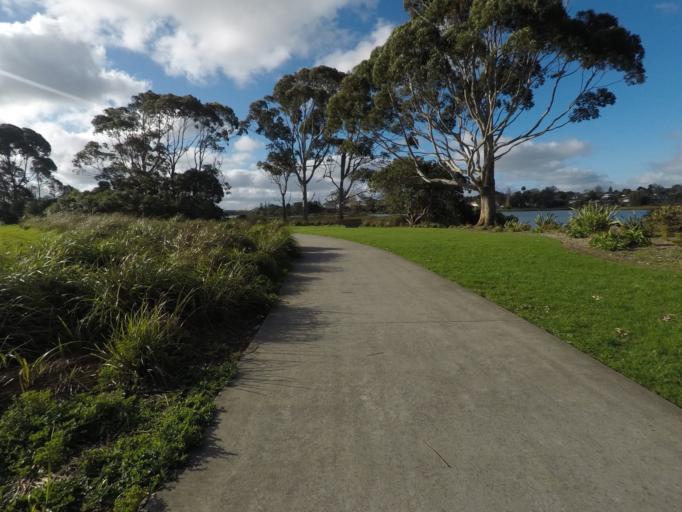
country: NZ
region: Auckland
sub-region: Auckland
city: Rosebank
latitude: -36.8933
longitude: 174.6716
